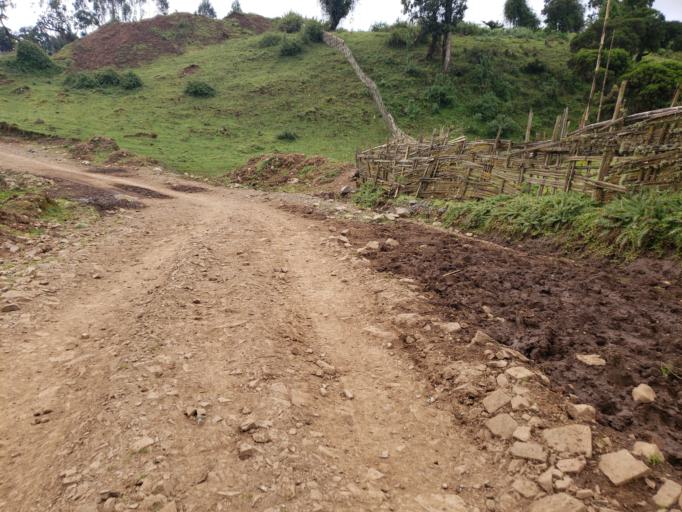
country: ET
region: Oromiya
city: Dodola
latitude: 6.7164
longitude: 39.3742
